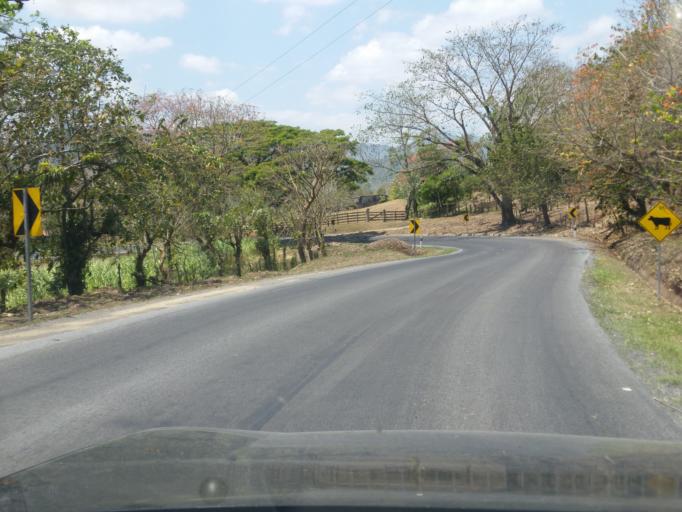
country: NI
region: Boaco
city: Boaco
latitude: 12.6032
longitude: -85.5393
